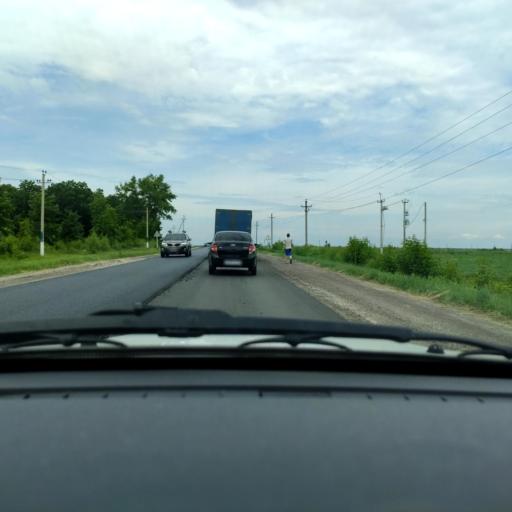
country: RU
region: Voronezj
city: Novaya Usman'
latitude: 51.6852
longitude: 39.3968
